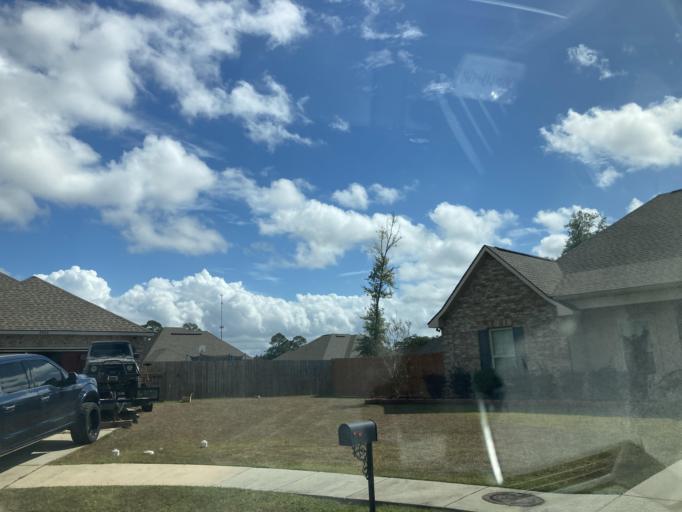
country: US
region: Mississippi
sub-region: Jackson County
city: Gulf Hills
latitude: 30.4527
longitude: -88.8244
